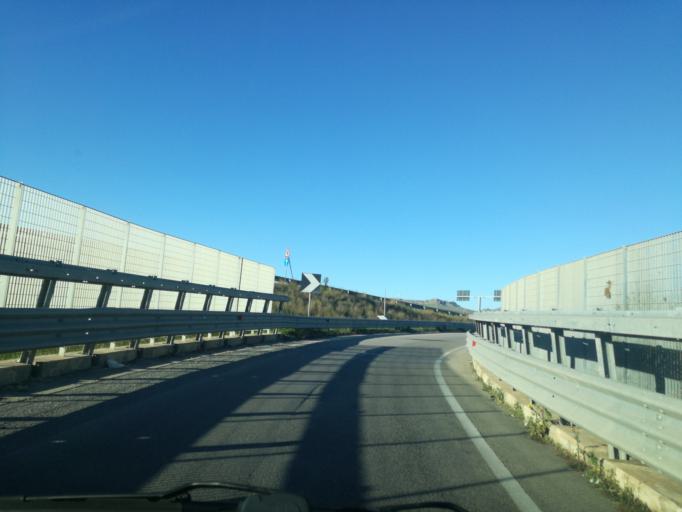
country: IT
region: Sicily
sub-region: Provincia di Caltanissetta
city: Butera
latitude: 37.1259
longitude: 14.1194
